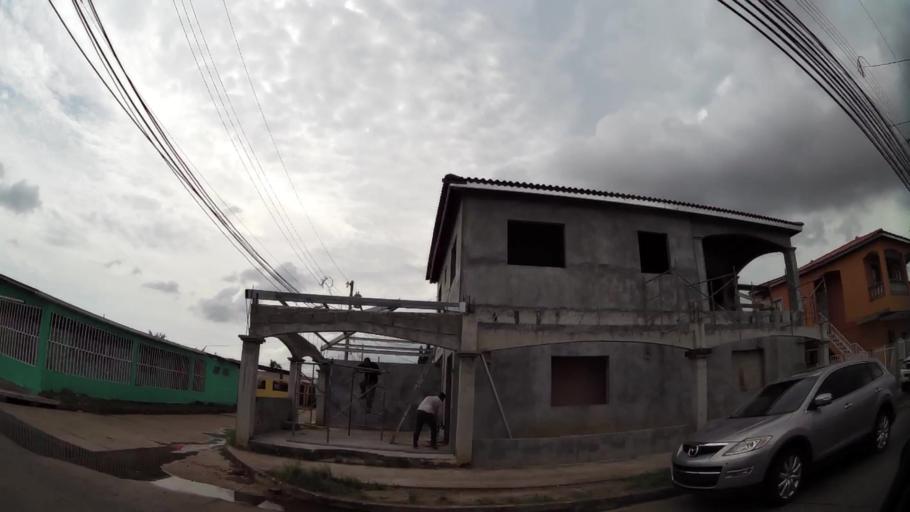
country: PA
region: Panama
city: Tocumen
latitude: 9.0463
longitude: -79.4116
